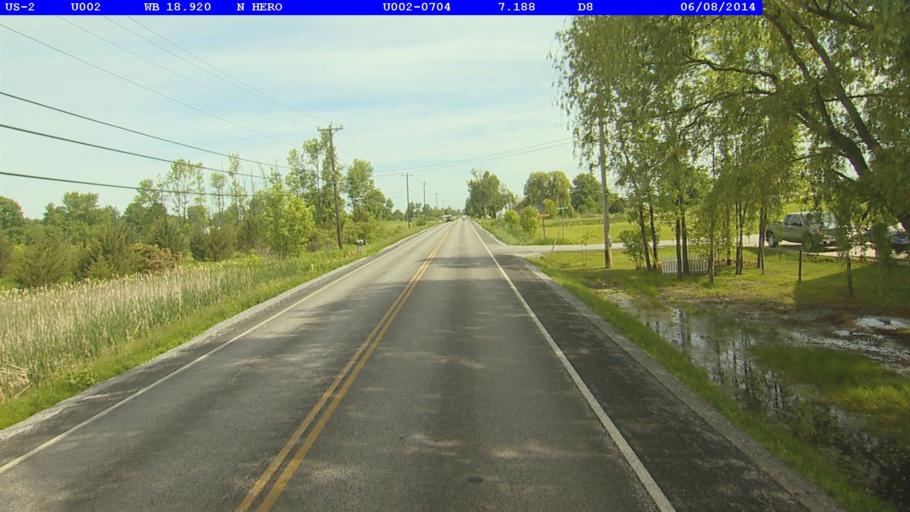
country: US
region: Vermont
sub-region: Grand Isle County
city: North Hero
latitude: 44.7961
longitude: -73.2923
